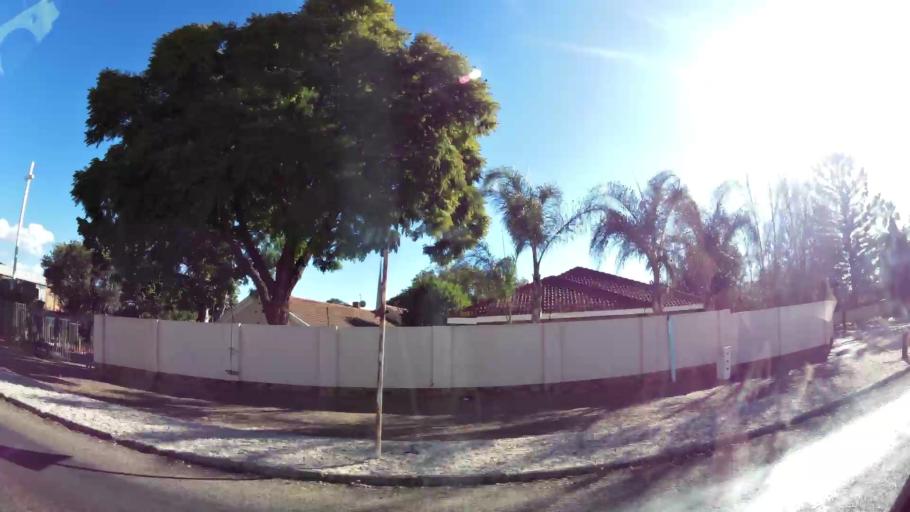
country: ZA
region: Limpopo
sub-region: Capricorn District Municipality
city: Polokwane
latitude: -23.9019
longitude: 29.4725
